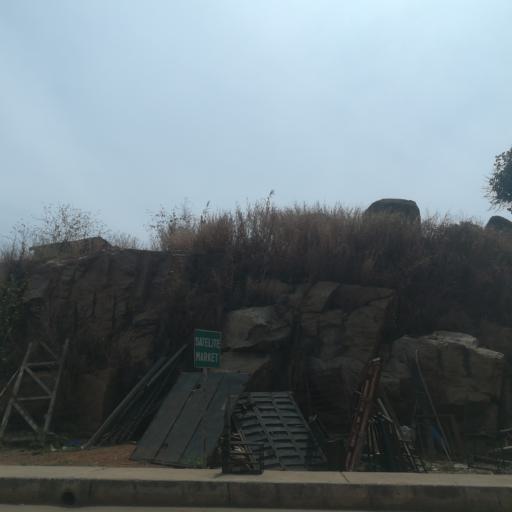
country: NG
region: Plateau
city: Jos
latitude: 9.9278
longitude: 8.8626
